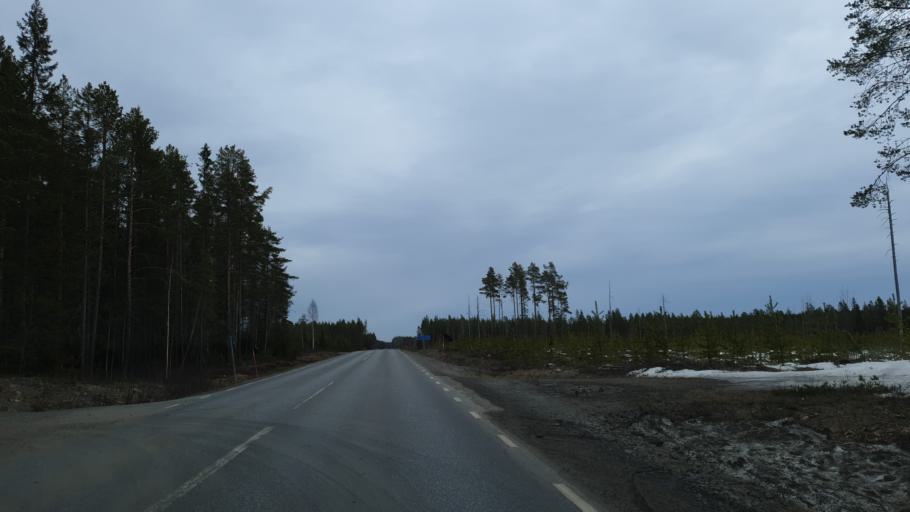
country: SE
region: Vaesterbotten
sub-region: Robertsfors Kommun
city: Robertsfors
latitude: 64.2052
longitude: 20.8662
